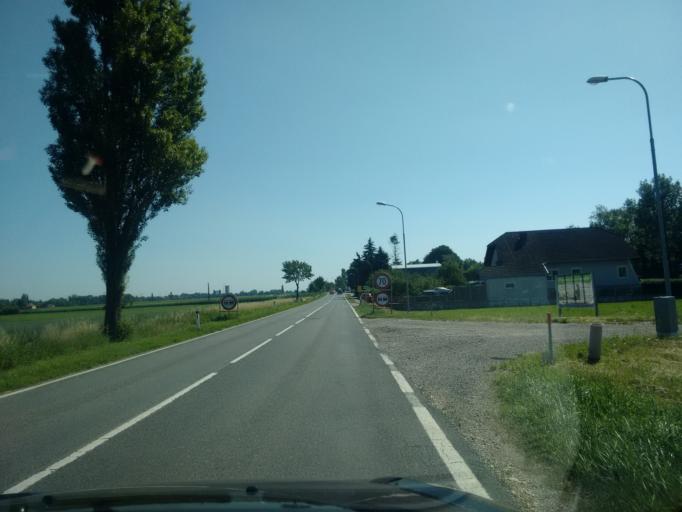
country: AT
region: Lower Austria
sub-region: Politischer Bezirk Tulln
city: Wurmla
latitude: 48.2767
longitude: 15.8789
